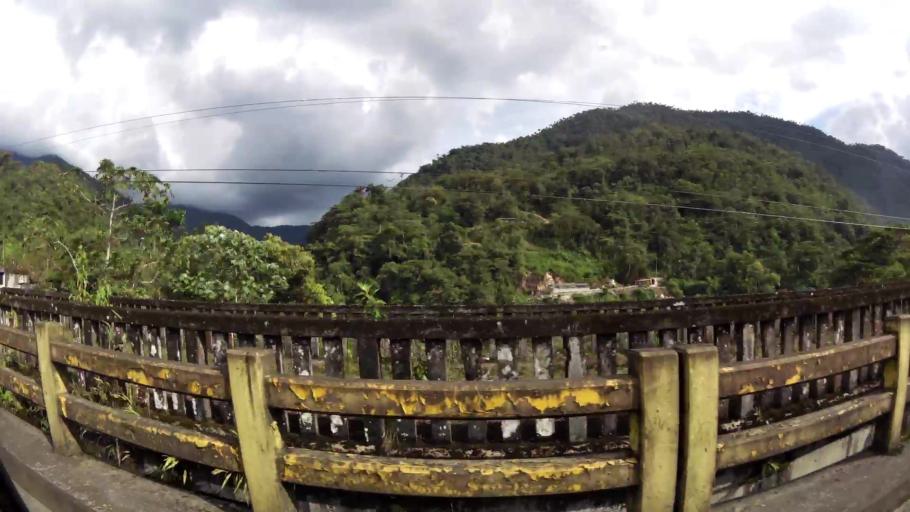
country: EC
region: Pastaza
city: Puyo
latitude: -1.4106
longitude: -78.1911
